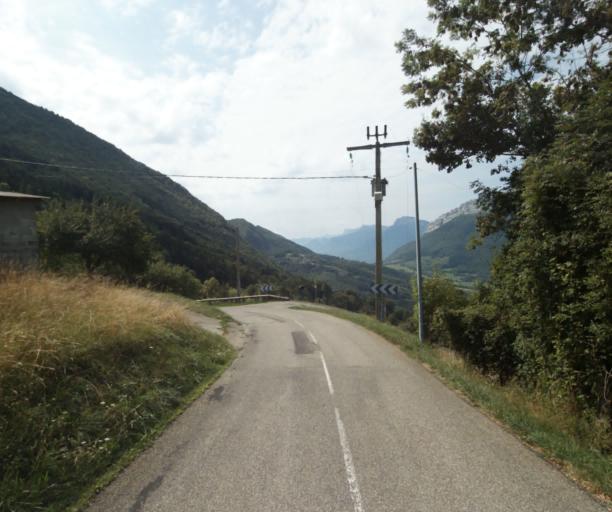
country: FR
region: Rhone-Alpes
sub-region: Departement de l'Isere
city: Le Sappey-en-Chartreuse
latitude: 45.2630
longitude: 5.7485
